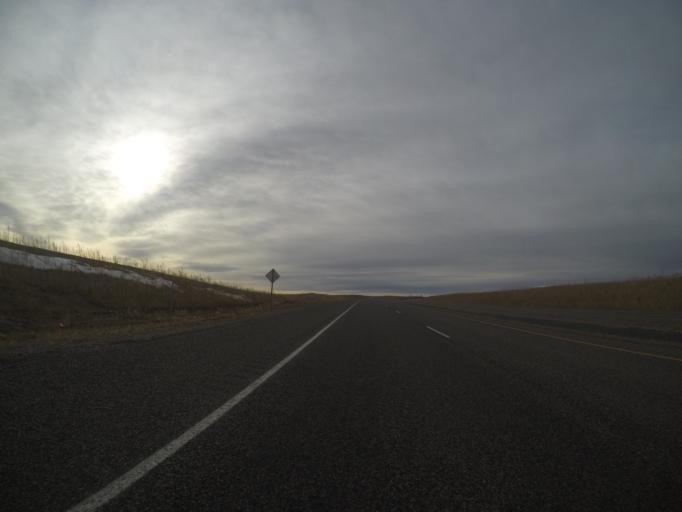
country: US
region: Montana
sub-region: Yellowstone County
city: Laurel
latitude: 45.5567
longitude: -108.8599
